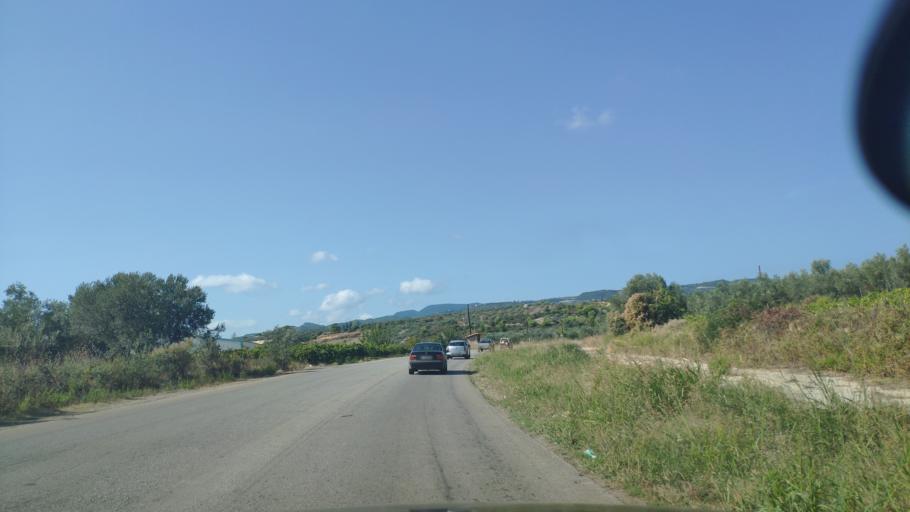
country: GR
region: Peloponnese
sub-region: Nomos Korinthias
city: Moulki
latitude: 37.9908
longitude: 22.6979
